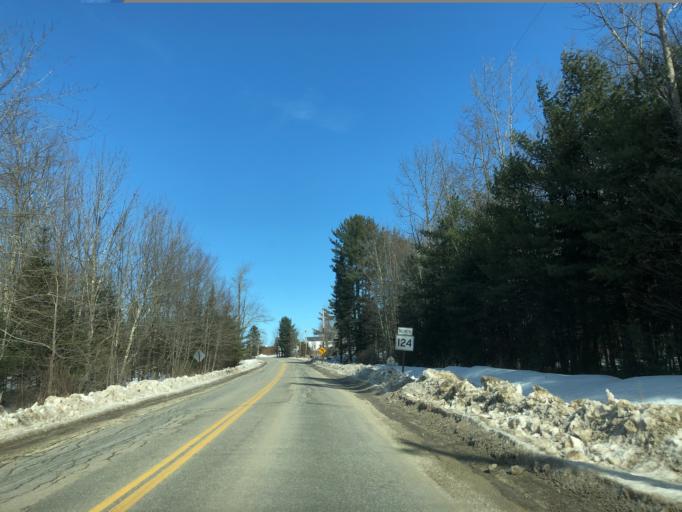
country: US
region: Maine
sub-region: Oxford County
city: Buckfield
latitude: 44.2323
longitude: -70.3362
